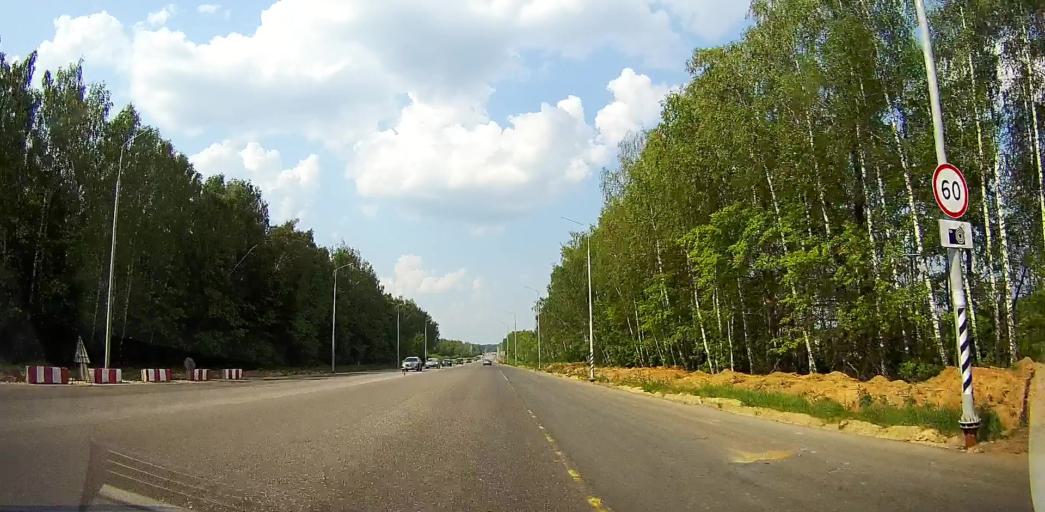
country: RU
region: Moskovskaya
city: Mikhnevo
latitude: 55.0594
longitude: 37.9548
